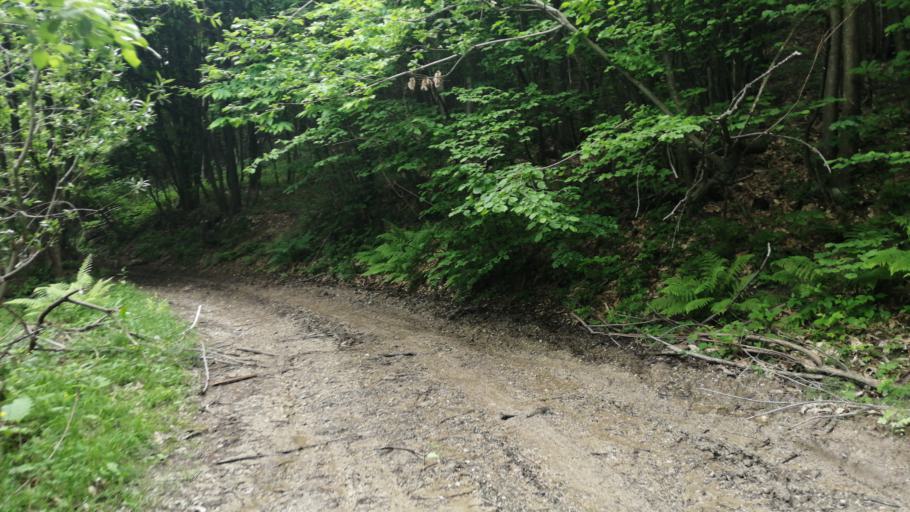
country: IT
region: Piedmont
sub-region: Provincia di Cuneo
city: Montaldo di Mondovi
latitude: 44.3152
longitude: 7.8627
